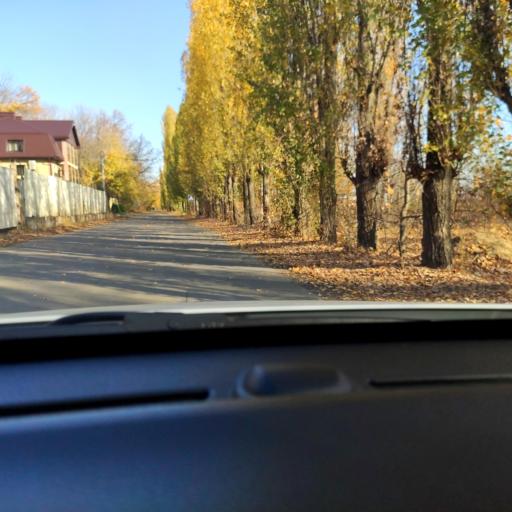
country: RU
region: Voronezj
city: Voronezh
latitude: 51.7026
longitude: 39.2370
